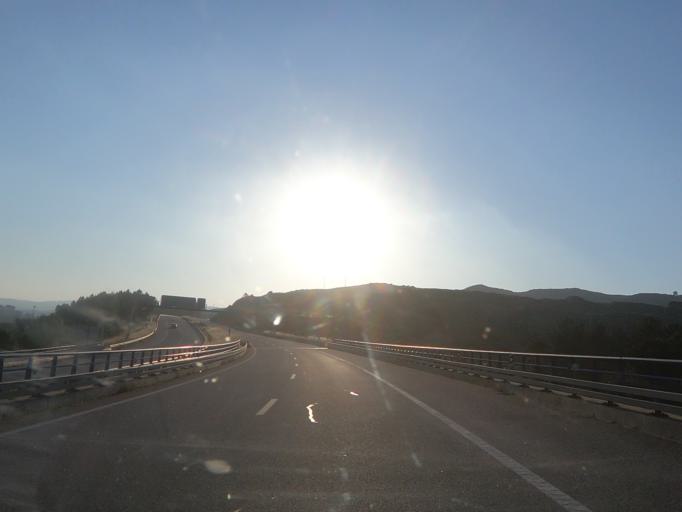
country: PT
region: Guarda
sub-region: Celorico da Beira
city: Celorico da Beira
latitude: 40.6320
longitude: -7.4329
